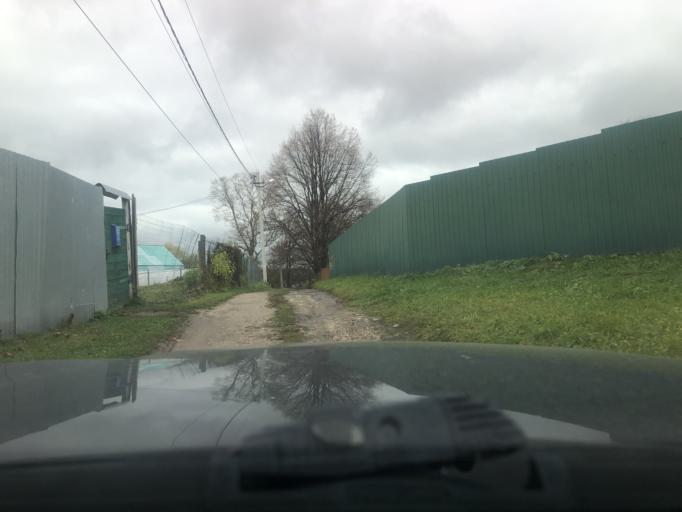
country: RU
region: Moskovskaya
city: Sergiyev Posad
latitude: 56.3021
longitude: 38.1215
